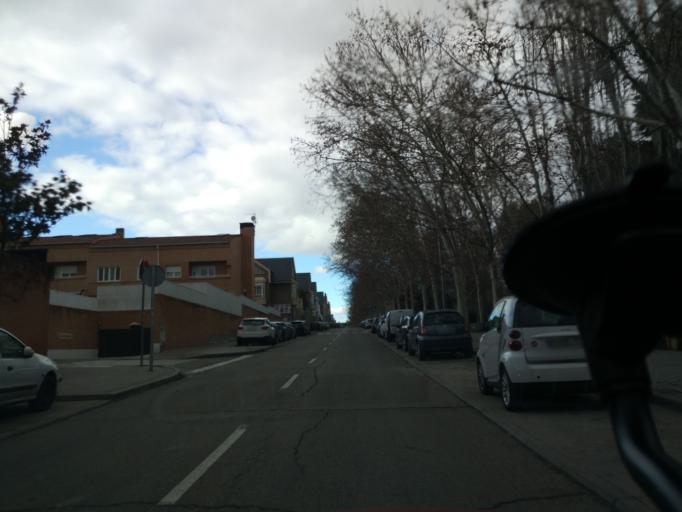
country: ES
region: Madrid
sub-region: Provincia de Madrid
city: San Blas
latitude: 40.4426
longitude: -3.6303
